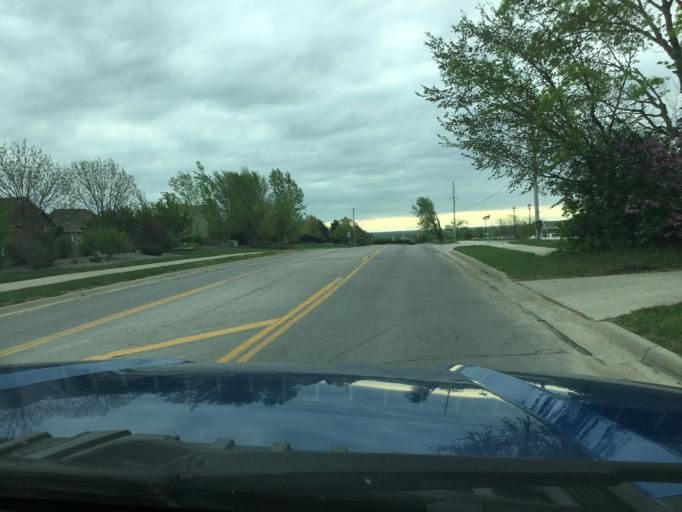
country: US
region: Kansas
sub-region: Douglas County
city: Lawrence
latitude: 38.9861
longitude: -95.2909
